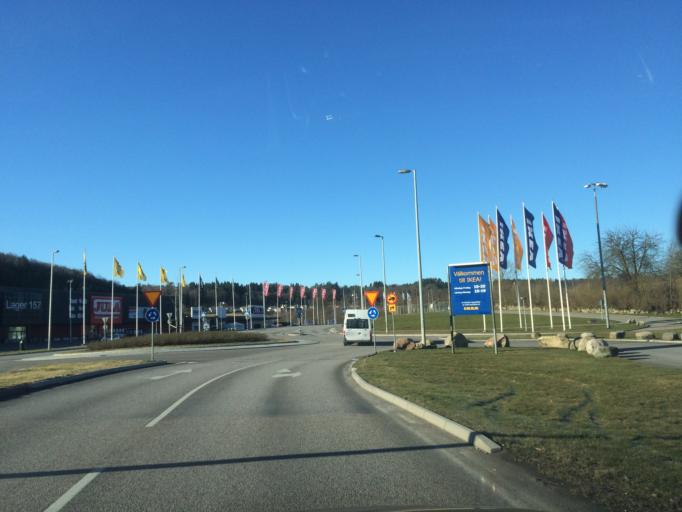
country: SE
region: Vaestra Goetaland
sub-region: Molndal
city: Kallered
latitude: 57.6024
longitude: 12.0511
